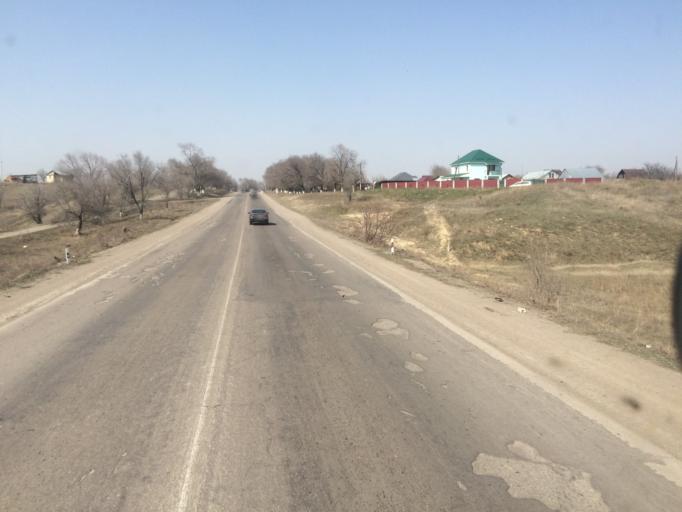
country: KZ
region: Almaty Oblysy
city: Burunday
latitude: 43.3052
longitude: 76.6702
